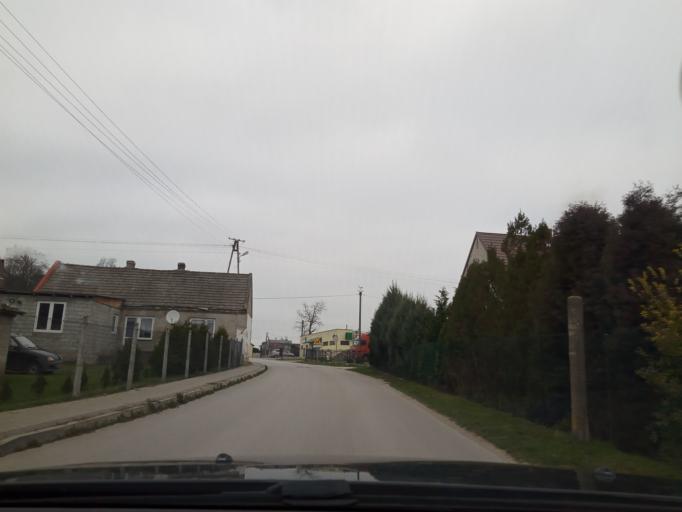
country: PL
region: Swietokrzyskie
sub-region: Powiat jedrzejowski
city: Imielno
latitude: 50.6026
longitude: 20.4908
